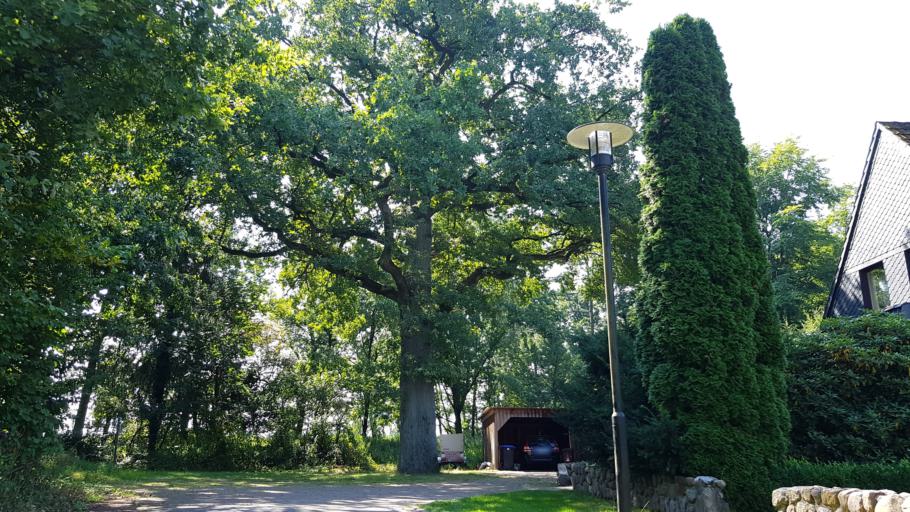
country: DE
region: Lower Saxony
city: Wendisch Evern
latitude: 53.2315
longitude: 10.4621
